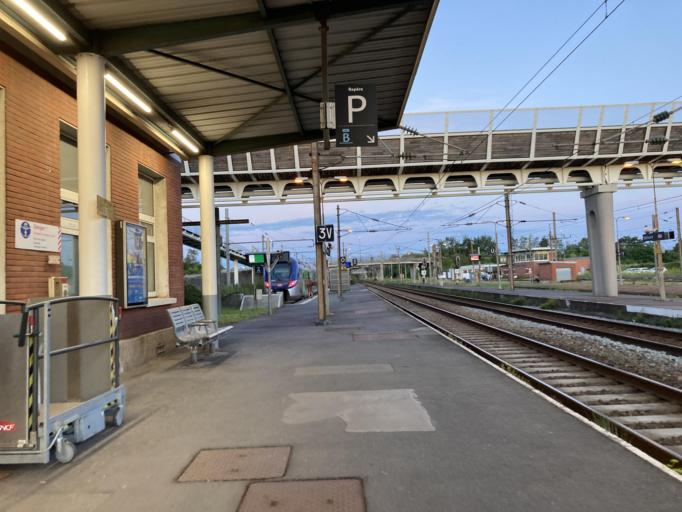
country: FR
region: Nord-Pas-de-Calais
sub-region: Departement du Pas-de-Calais
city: Bethune
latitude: 50.5212
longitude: 2.6405
